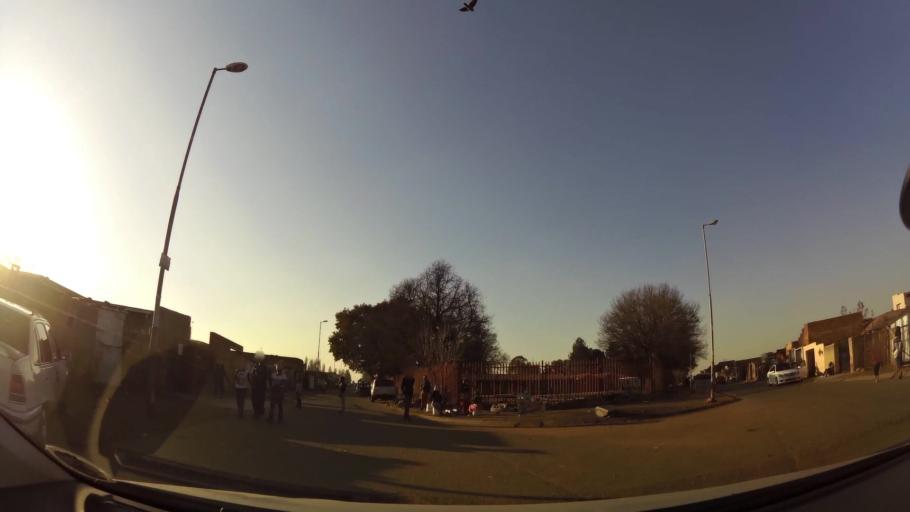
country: ZA
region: Gauteng
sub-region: City of Johannesburg Metropolitan Municipality
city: Soweto
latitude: -26.2560
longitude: 27.8786
